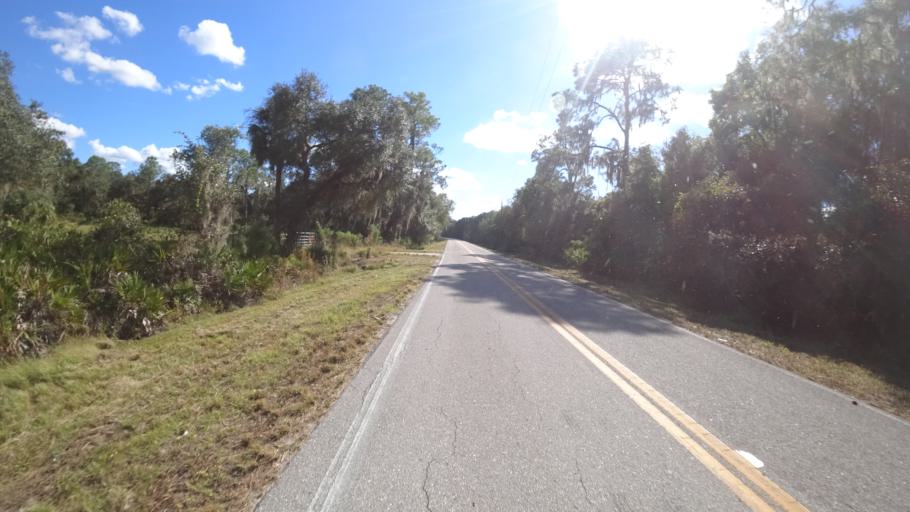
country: US
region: Florida
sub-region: Sarasota County
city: North Port
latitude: 27.2170
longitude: -82.1217
